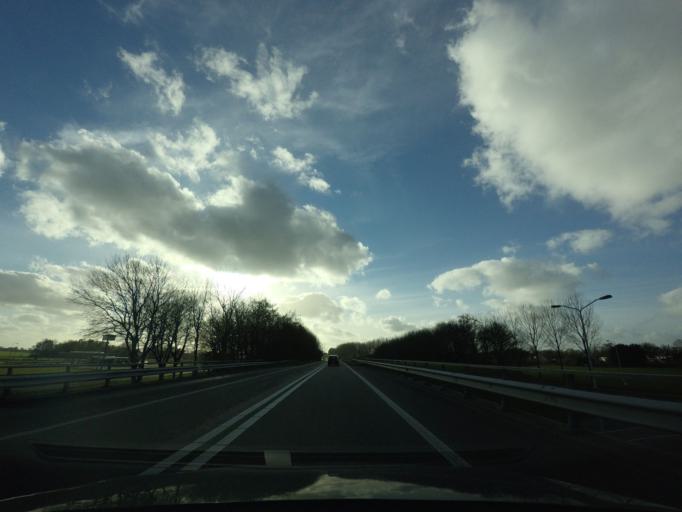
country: NL
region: North Holland
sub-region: Gemeente Opmeer
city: Opmeer
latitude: 52.7434
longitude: 4.9097
